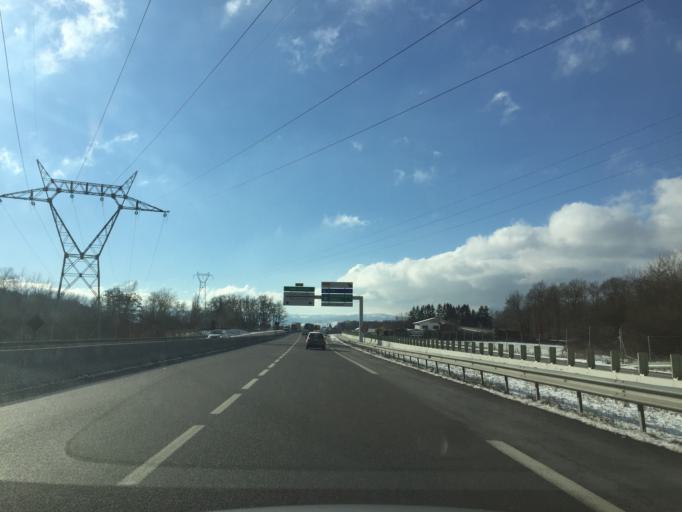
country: FR
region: Rhone-Alpes
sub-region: Departement de la Haute-Savoie
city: Cranves-Sales
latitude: 46.2102
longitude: 6.2954
